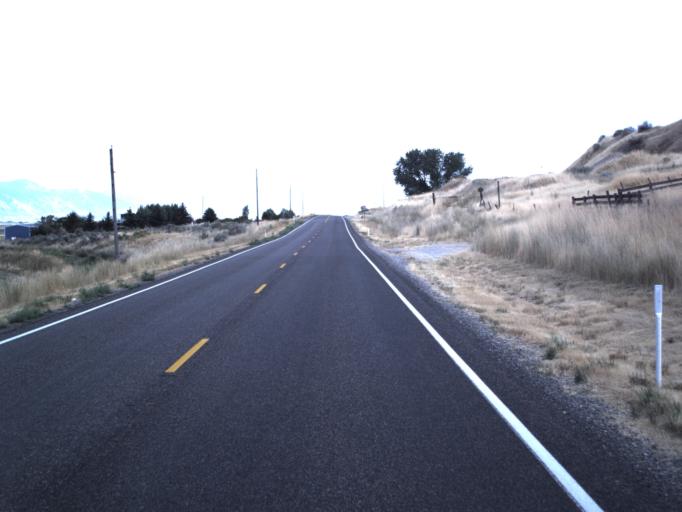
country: US
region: Utah
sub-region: Cache County
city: Benson
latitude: 41.8973
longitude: -111.9503
